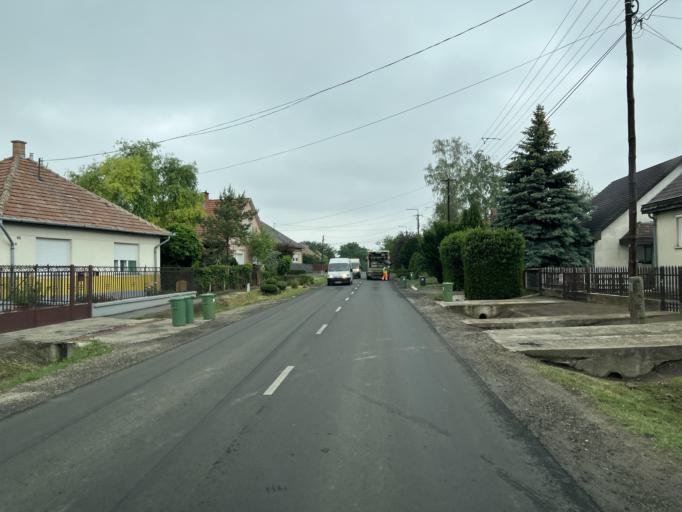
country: HU
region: Pest
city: Zsambok
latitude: 47.5537
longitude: 19.6048
